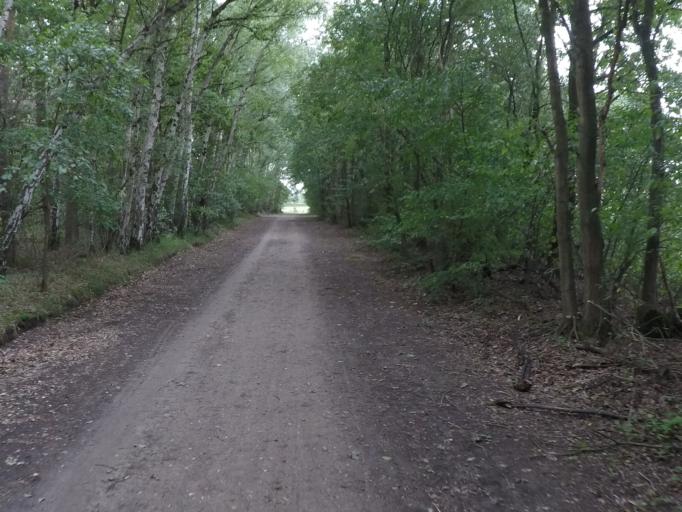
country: BE
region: Flanders
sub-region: Provincie Antwerpen
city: Vorselaar
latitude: 51.2098
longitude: 4.7726
